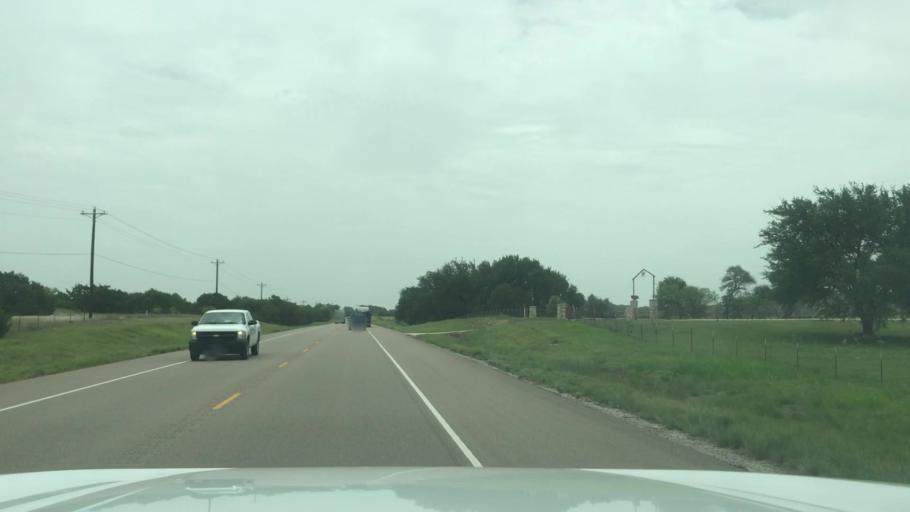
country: US
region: Texas
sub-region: Bosque County
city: Meridian
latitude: 31.9418
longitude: -97.7133
